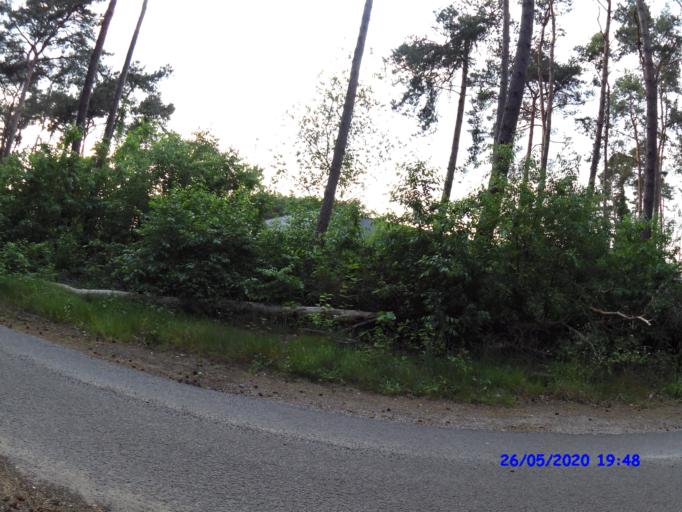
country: BE
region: Flanders
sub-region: Provincie Antwerpen
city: Vorselaar
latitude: 51.1729
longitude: 4.7934
